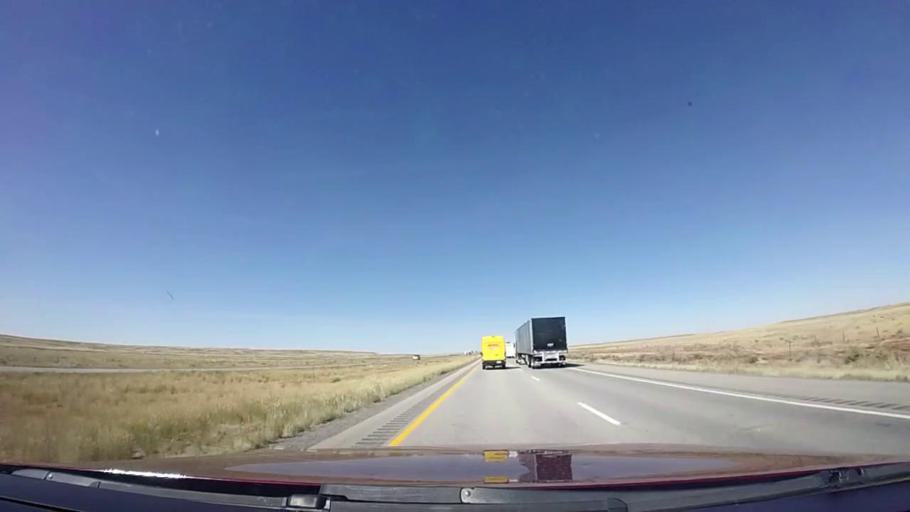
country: US
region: Wyoming
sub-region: Carbon County
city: Rawlins
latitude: 41.6625
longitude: -108.0548
